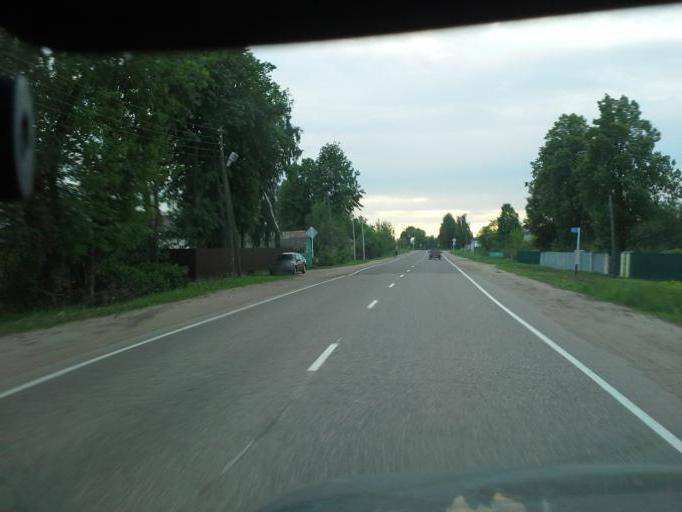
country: RU
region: Ivanovo
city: Gavrilov Posad
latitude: 56.5595
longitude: 40.1450
